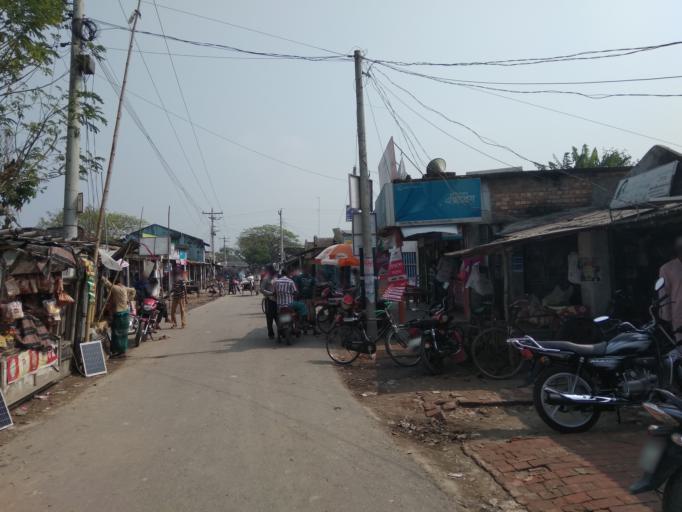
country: IN
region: West Bengal
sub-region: North 24 Parganas
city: Gosaba
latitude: 22.2282
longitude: 89.1550
